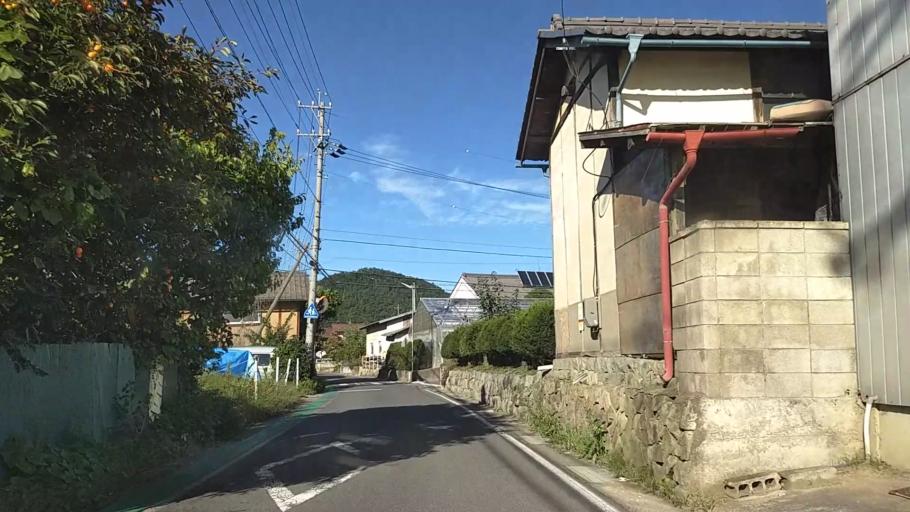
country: JP
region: Nagano
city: Nagano-shi
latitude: 36.5492
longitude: 138.1552
